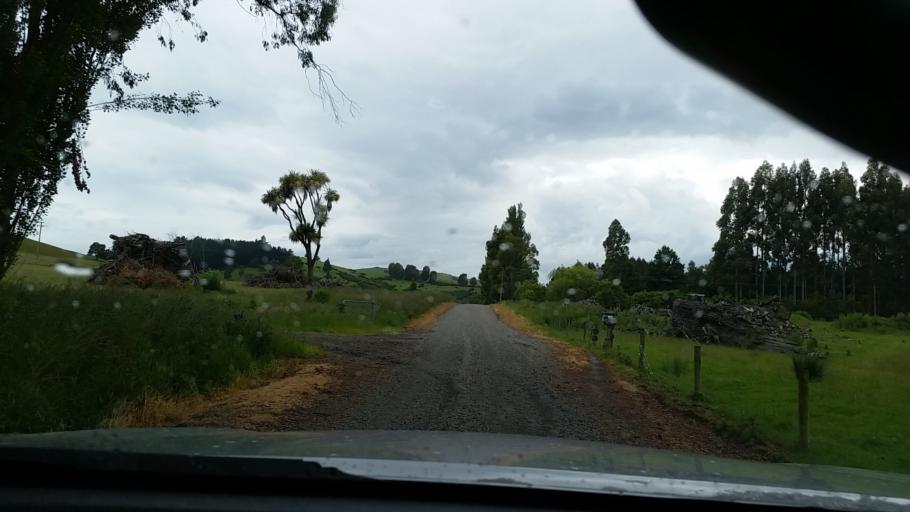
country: NZ
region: Southland
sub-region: Southland District
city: Winton
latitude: -45.9752
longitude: 168.1486
